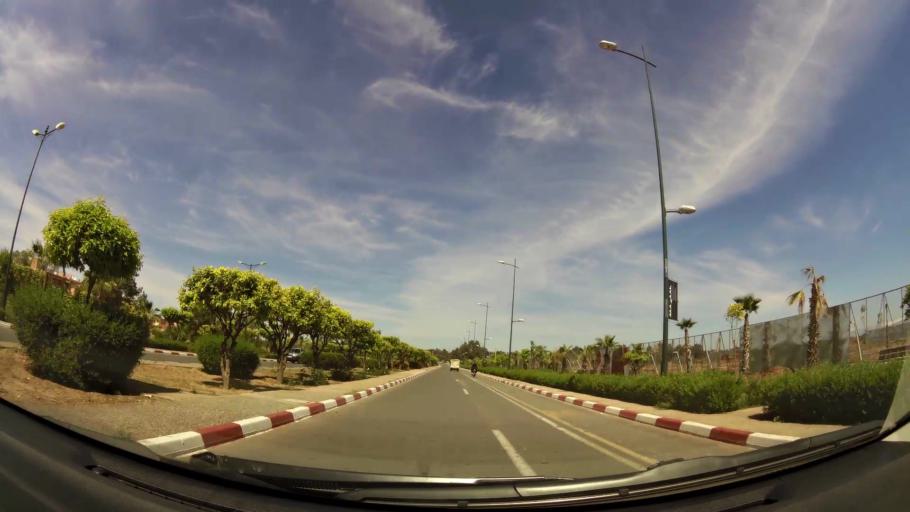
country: MA
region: Marrakech-Tensift-Al Haouz
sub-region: Marrakech
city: Marrakesh
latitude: 31.6046
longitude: -7.9582
